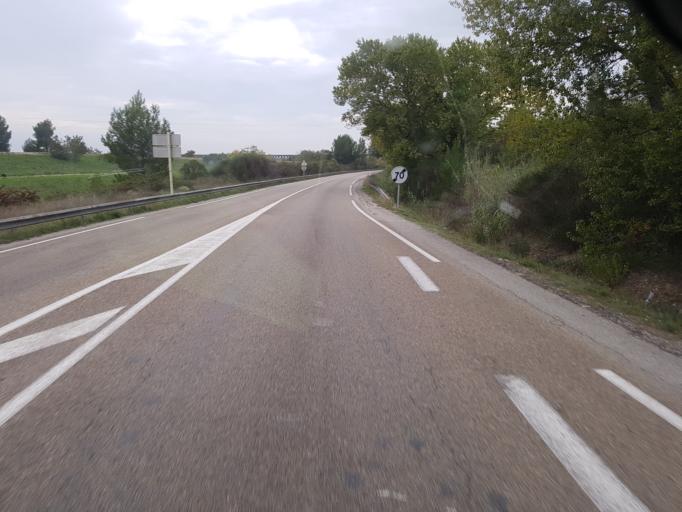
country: FR
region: Provence-Alpes-Cote d'Azur
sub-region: Departement du Vaucluse
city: Avignon
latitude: 43.9460
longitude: 4.7848
